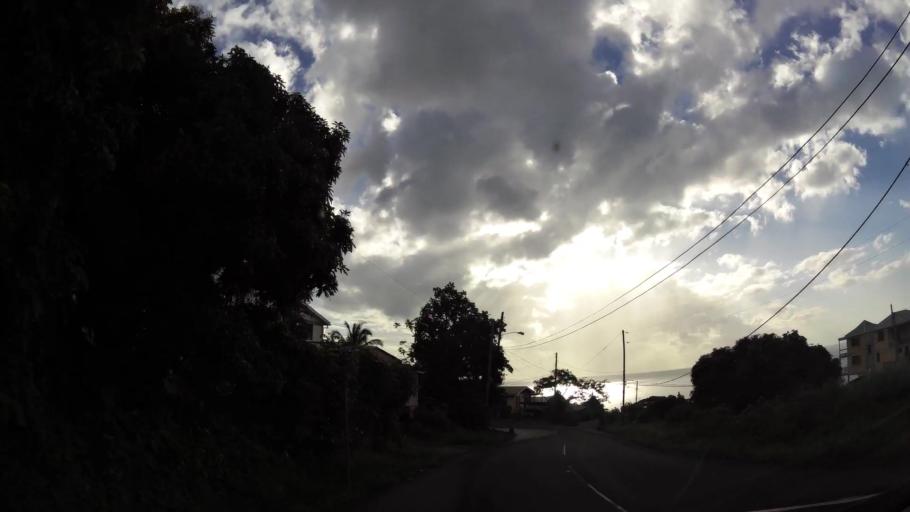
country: DM
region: Saint Paul
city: Mahaut
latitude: 15.3380
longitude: -61.3866
